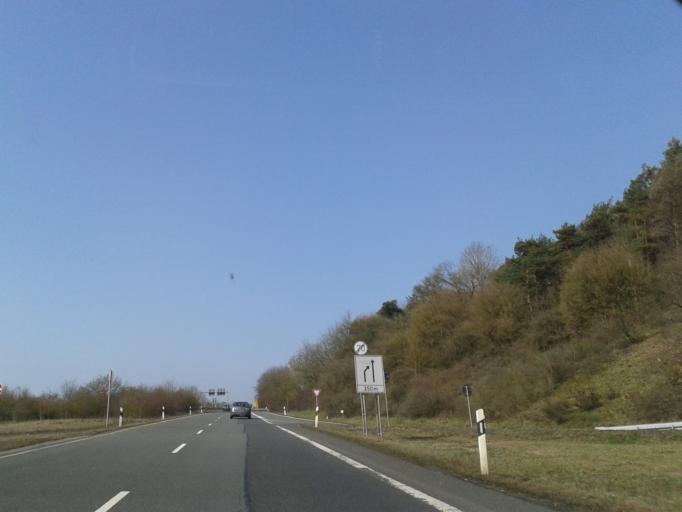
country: DE
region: Hesse
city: Herborn
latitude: 50.6772
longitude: 8.2825
